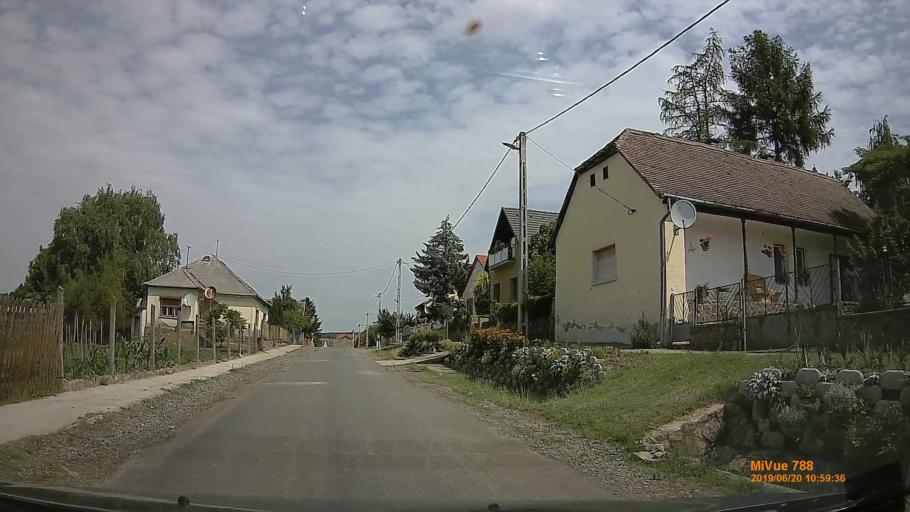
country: HU
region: Baranya
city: Mecseknadasd
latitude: 46.1687
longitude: 18.5134
